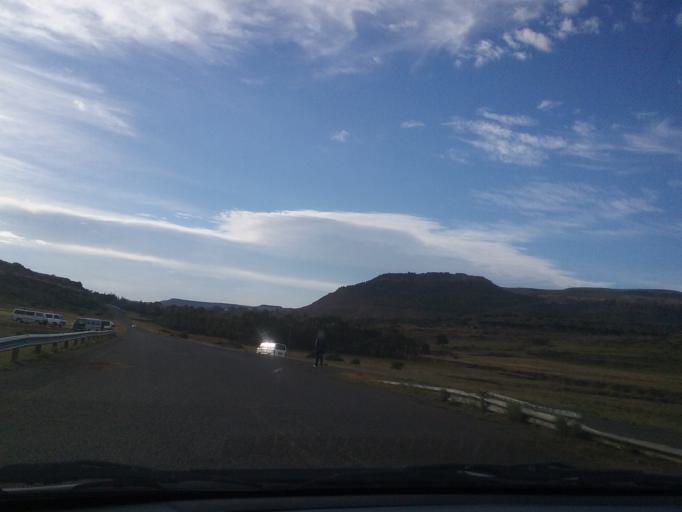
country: LS
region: Quthing
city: Quthing
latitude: -30.3876
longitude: 27.6049
